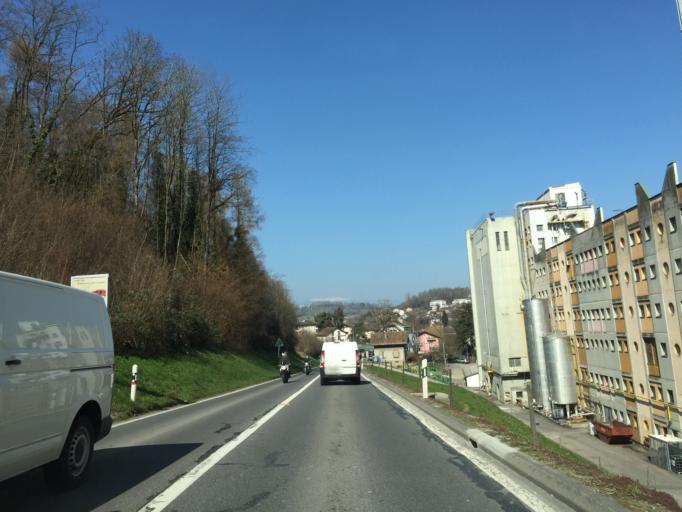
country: CH
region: Vaud
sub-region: Gros-de-Vaud District
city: Penthalaz
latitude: 46.6043
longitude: 6.5225
